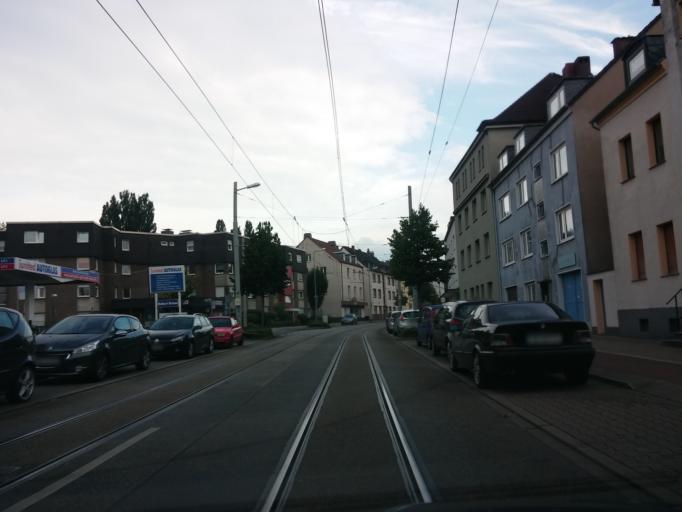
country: DE
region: North Rhine-Westphalia
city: Herten
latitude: 51.5646
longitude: 7.0837
